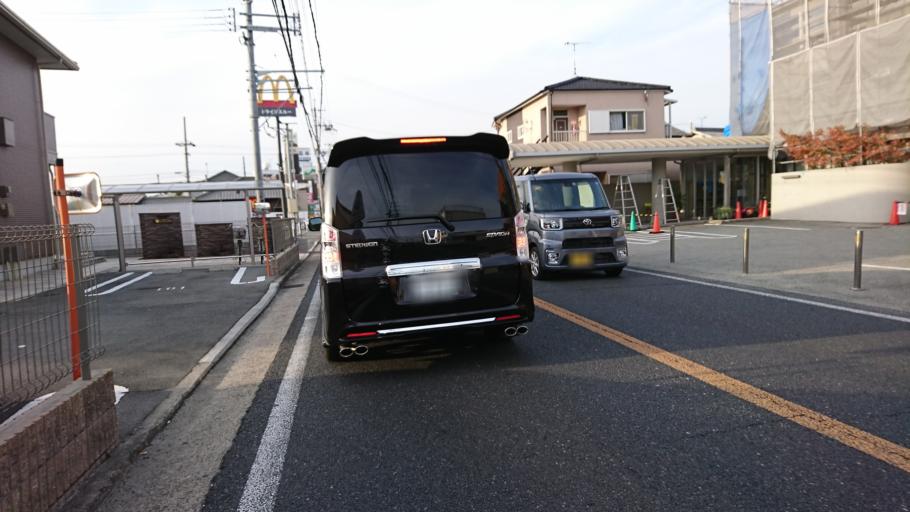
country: JP
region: Hyogo
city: Kakogawacho-honmachi
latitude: 34.7391
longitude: 134.8251
